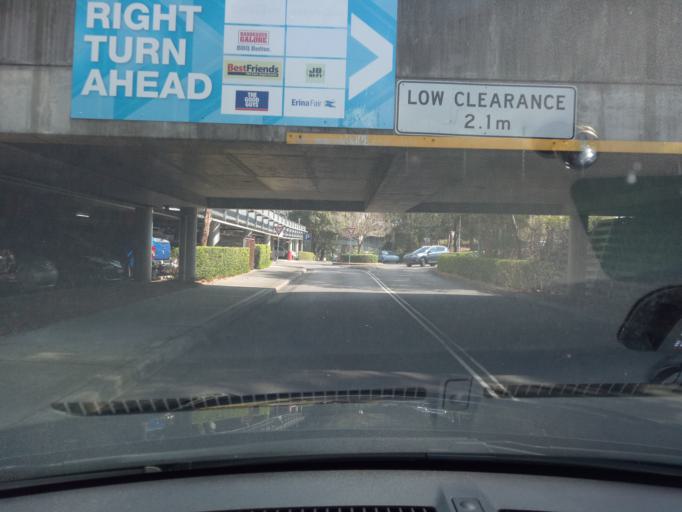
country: AU
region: New South Wales
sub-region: Gosford Shire
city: Erina
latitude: -33.4360
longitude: 151.3918
